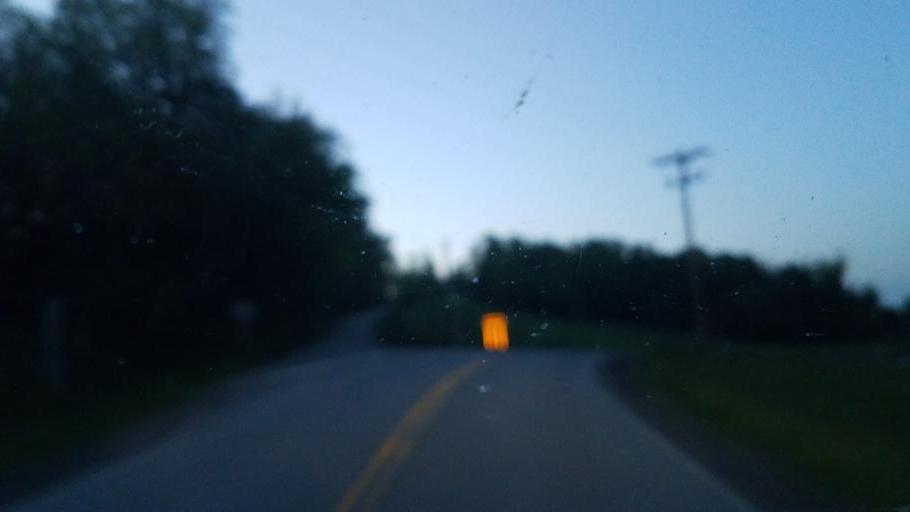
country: US
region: Ohio
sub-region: Belmont County
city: Barnesville
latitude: 40.0874
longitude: -81.3205
